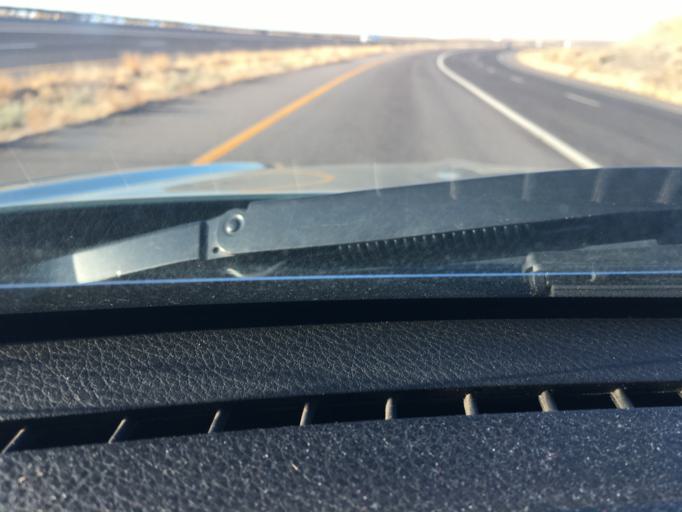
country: US
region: Colorado
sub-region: Delta County
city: Delta
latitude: 38.7516
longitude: -108.1577
